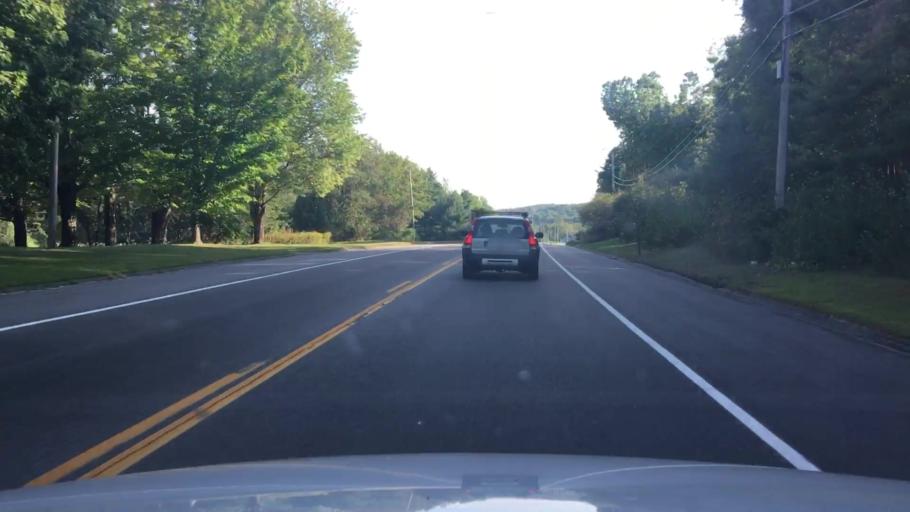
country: US
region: Maine
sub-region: Cumberland County
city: Cumberland Center
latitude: 43.7645
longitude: -70.3010
